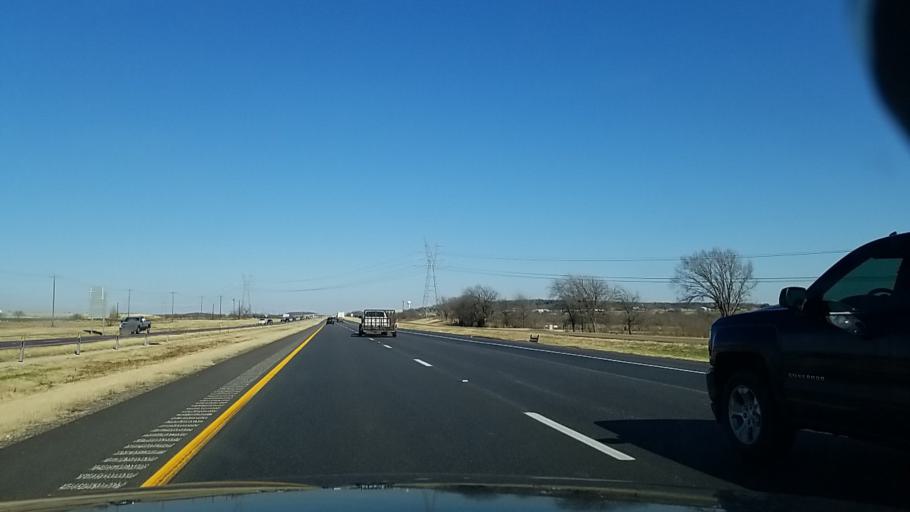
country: US
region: Texas
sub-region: Denton County
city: Argyle
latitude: 33.1034
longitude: -97.2226
